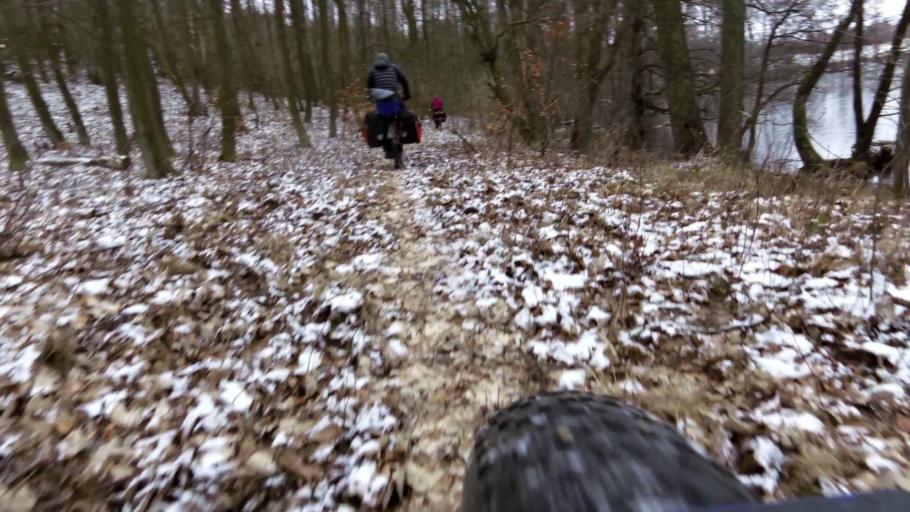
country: PL
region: West Pomeranian Voivodeship
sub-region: Powiat walecki
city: Miroslawiec
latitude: 53.3504
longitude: 16.2655
